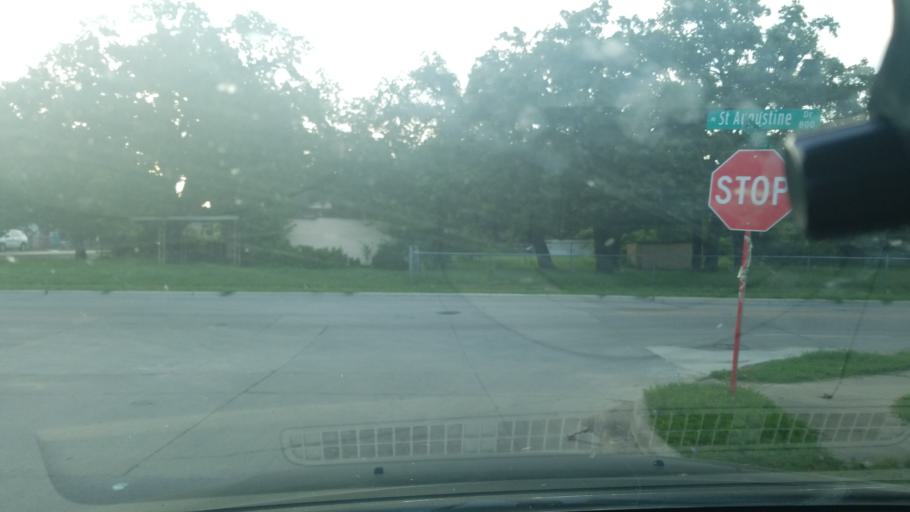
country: US
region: Texas
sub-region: Dallas County
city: Balch Springs
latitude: 32.7275
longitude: -96.6572
